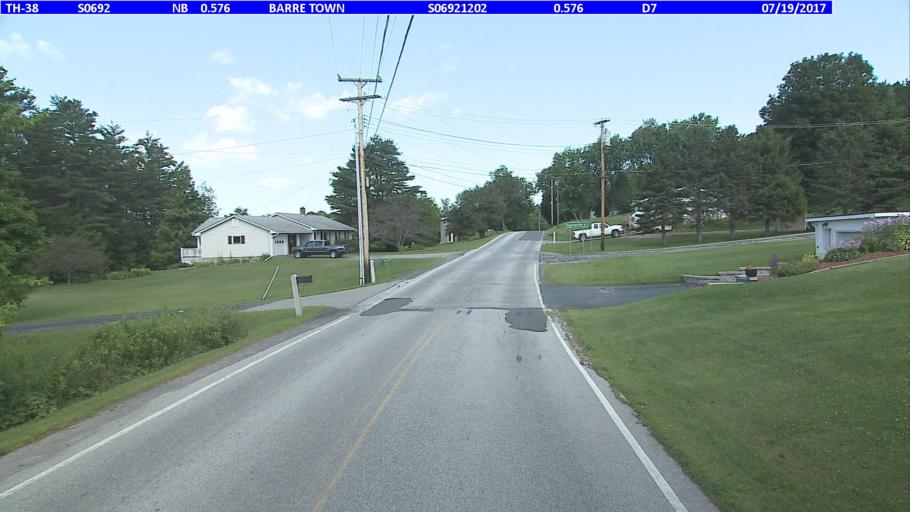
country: US
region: Vermont
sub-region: Washington County
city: South Barre
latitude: 44.1676
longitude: -72.4519
